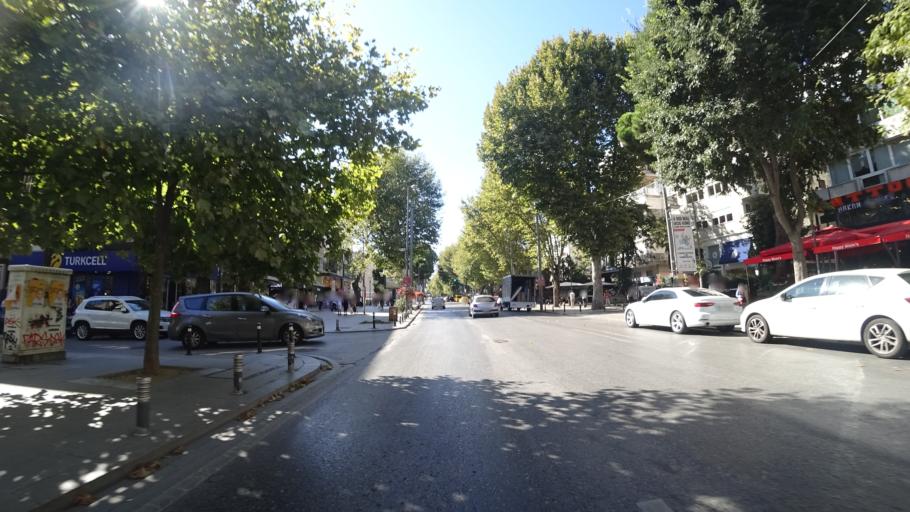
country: TR
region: Istanbul
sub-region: Atasehir
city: Atasehir
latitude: 40.9643
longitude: 29.0733
